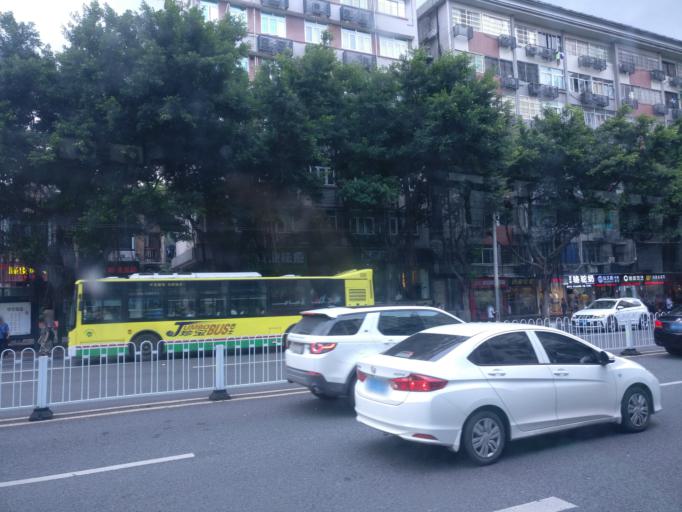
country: CN
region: Guangdong
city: Guangzhou
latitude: 23.1294
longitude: 113.2801
